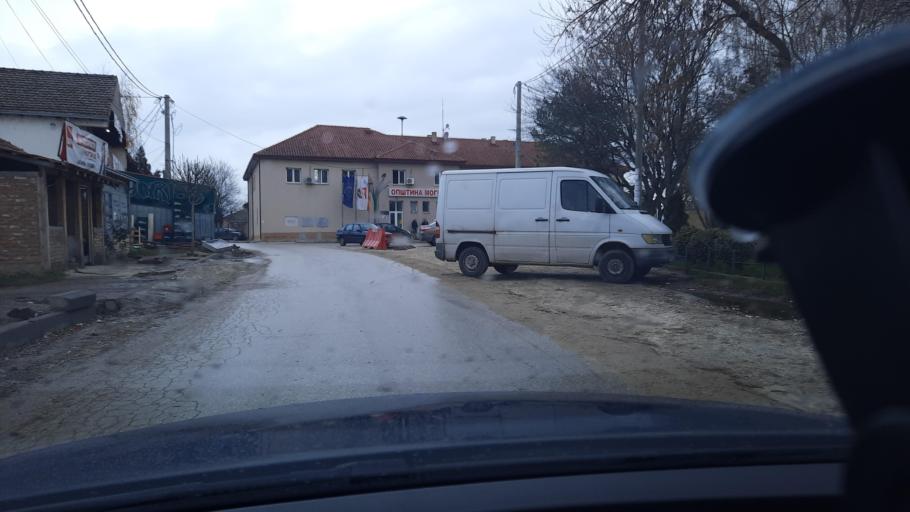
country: MK
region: Mogila
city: Mogila
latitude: 41.1075
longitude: 21.3780
